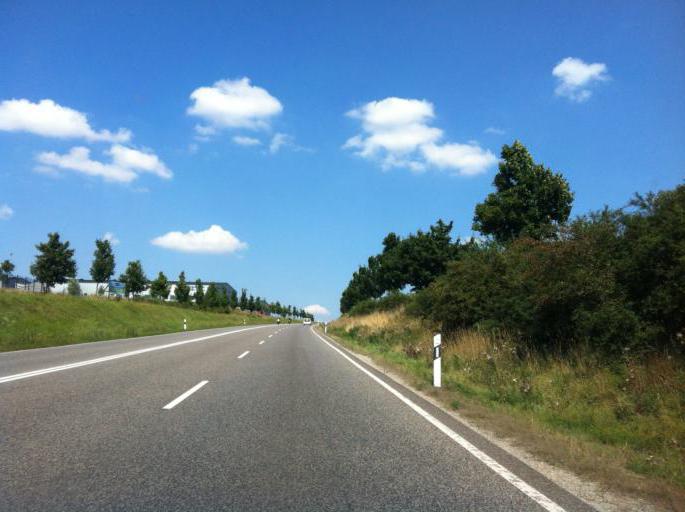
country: DE
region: Thuringia
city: Heilbad Heiligenstadt
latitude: 51.3882
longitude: 10.1307
